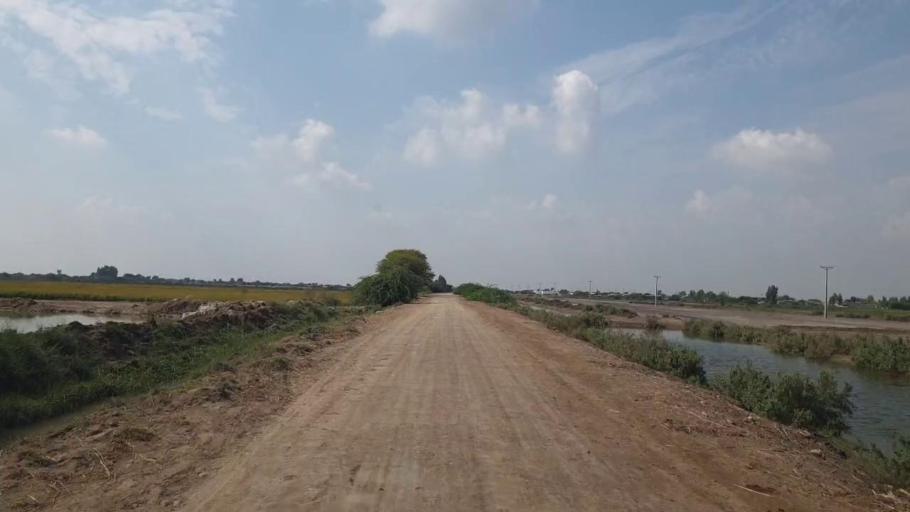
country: PK
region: Sindh
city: Badin
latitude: 24.5065
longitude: 68.6504
